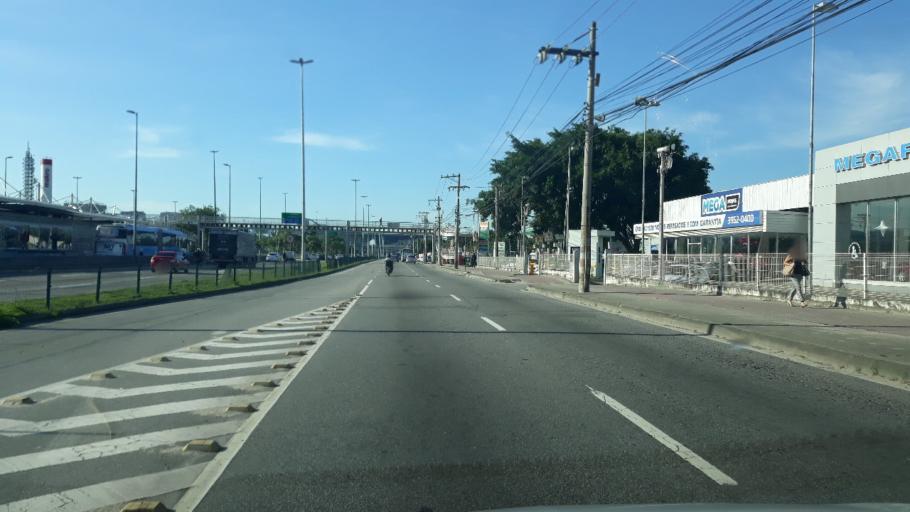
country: BR
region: Rio de Janeiro
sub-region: Rio De Janeiro
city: Rio de Janeiro
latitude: -22.9885
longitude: -43.3661
